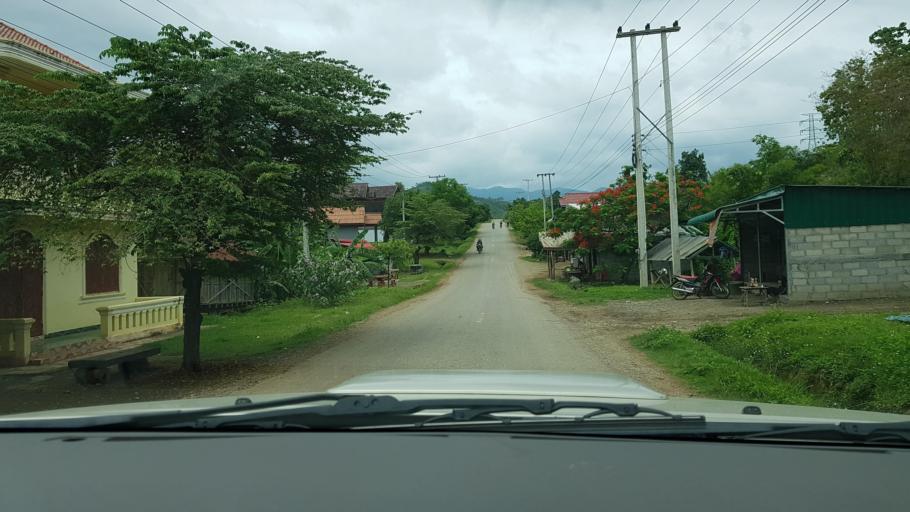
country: TH
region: Nan
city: Chaloem Phra Kiat
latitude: 19.9892
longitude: 101.2773
